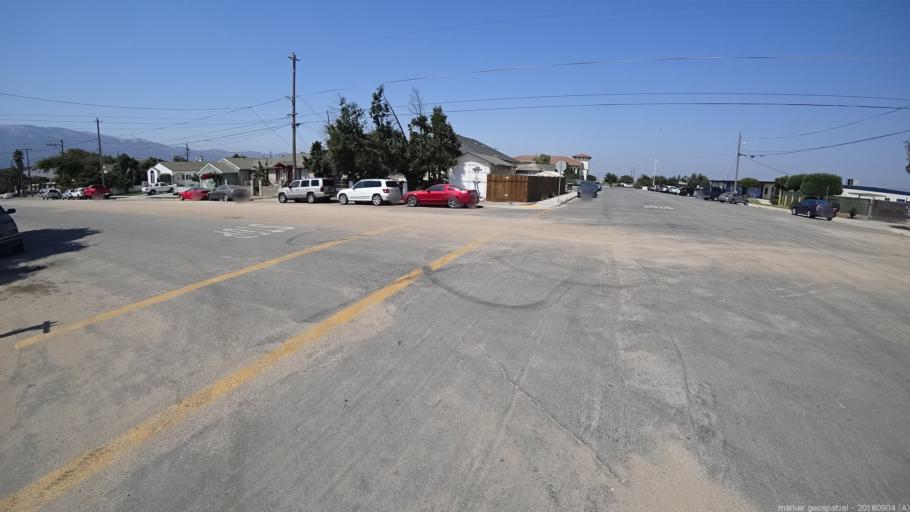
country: US
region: California
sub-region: Monterey County
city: Chualar
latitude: 36.5708
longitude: -121.5157
